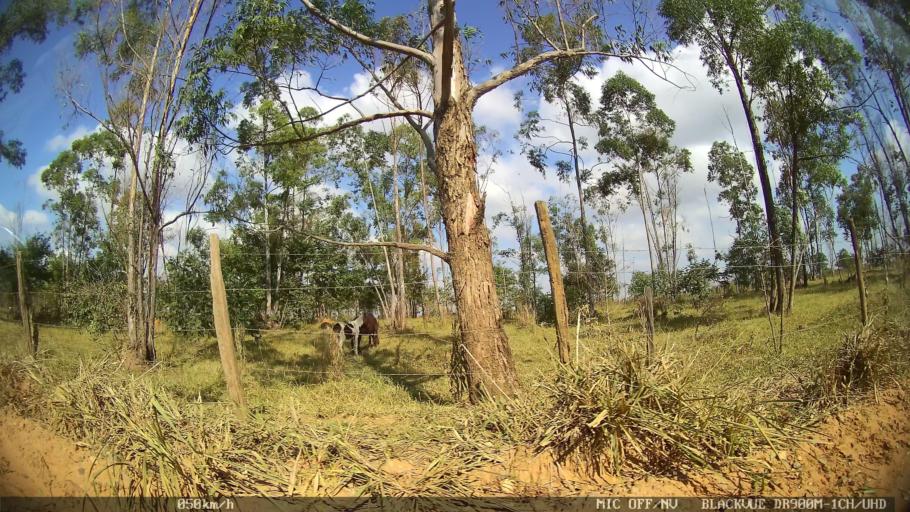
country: BR
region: Sao Paulo
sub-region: Indaiatuba
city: Indaiatuba
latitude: -22.9971
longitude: -47.2087
